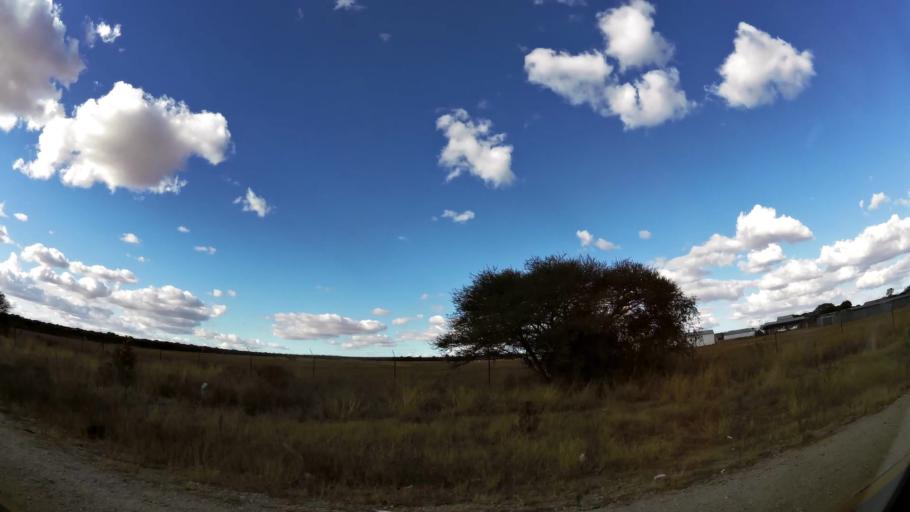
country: ZA
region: Limpopo
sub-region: Capricorn District Municipality
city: Polokwane
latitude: -23.9322
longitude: 29.4725
